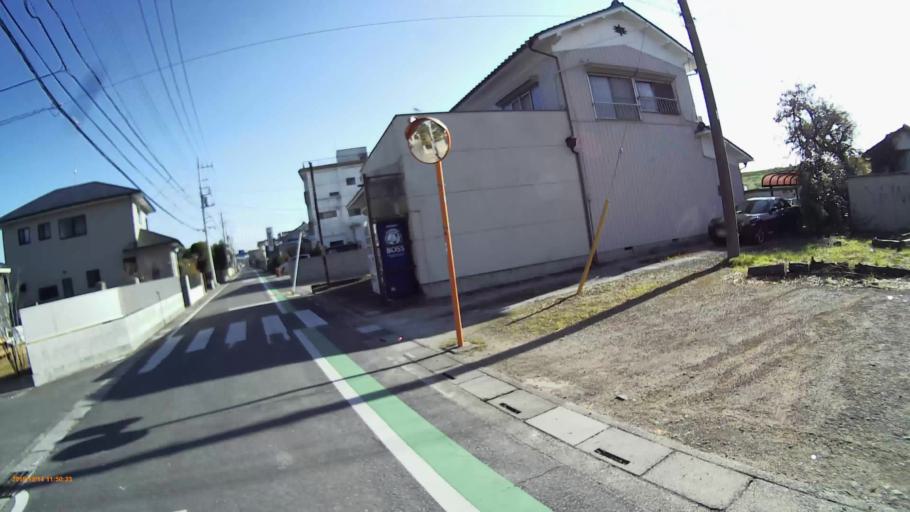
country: JP
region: Saitama
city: Kumagaya
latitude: 36.1227
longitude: 139.4073
